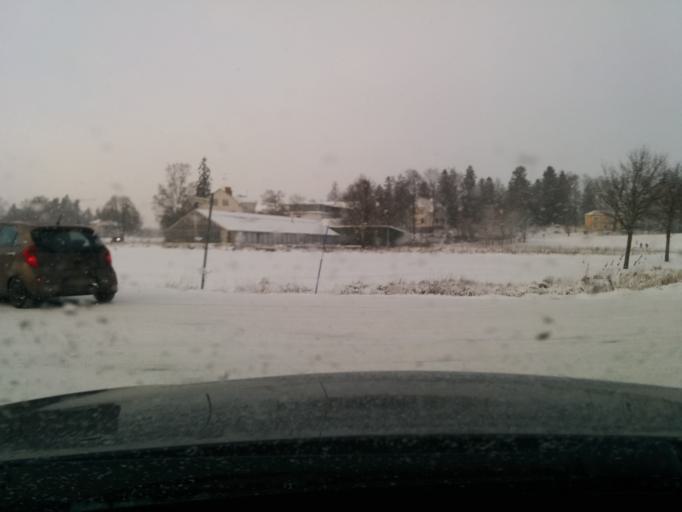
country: SE
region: Uppsala
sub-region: Tierps Kommun
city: Orbyhus
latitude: 60.2250
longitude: 17.7083
